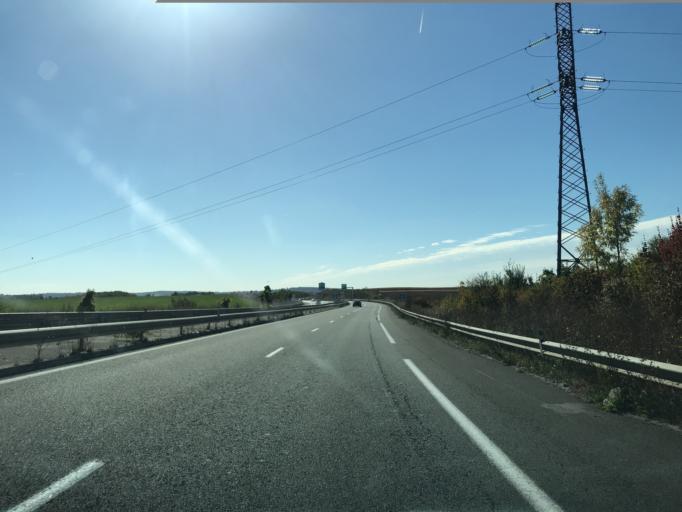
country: FR
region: Ile-de-France
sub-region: Departement de Seine-et-Marne
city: Villenoy
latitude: 48.9449
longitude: 2.8531
